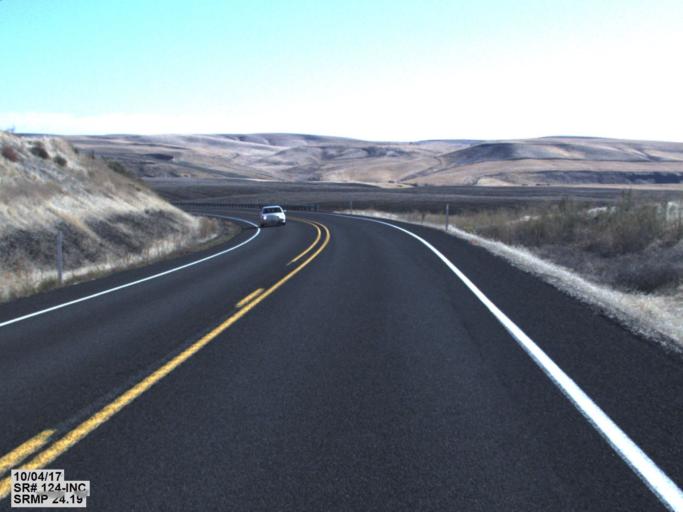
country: US
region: Washington
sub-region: Walla Walla County
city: Garrett
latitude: 46.2894
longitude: -118.5550
